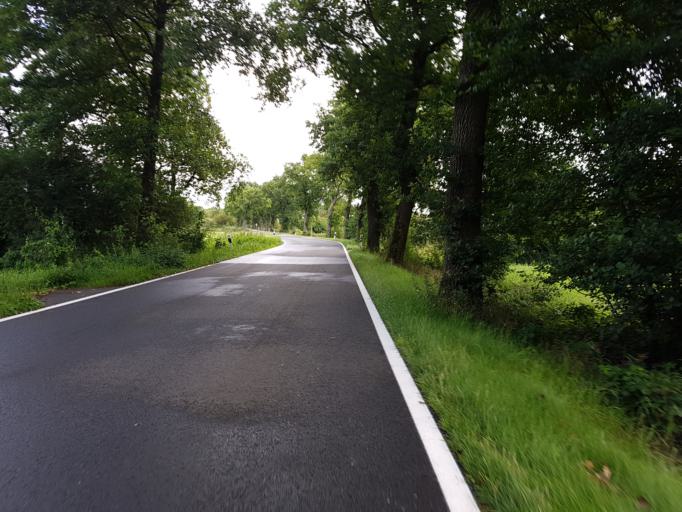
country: DE
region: Lower Saxony
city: Wittmund
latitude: 53.5254
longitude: 7.7277
